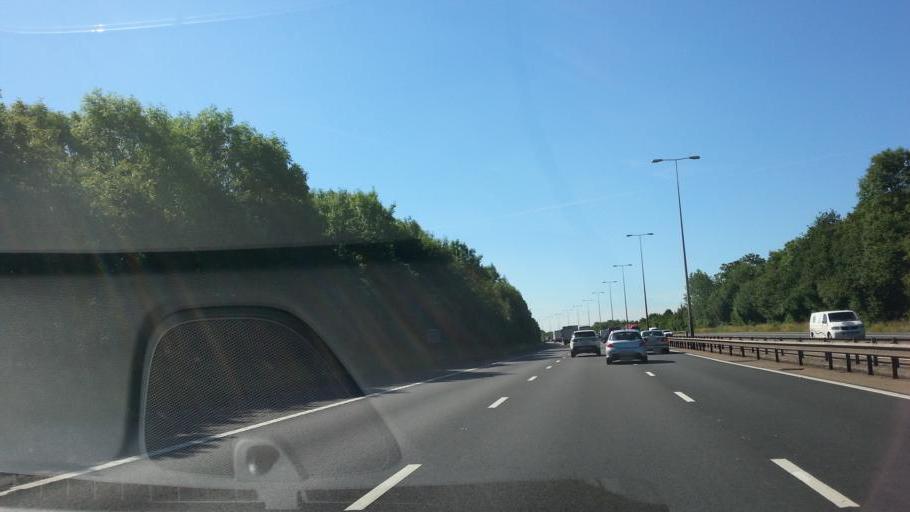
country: GB
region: England
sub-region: Worcestershire
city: Upton upon Severn
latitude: 52.0985
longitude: -2.1862
